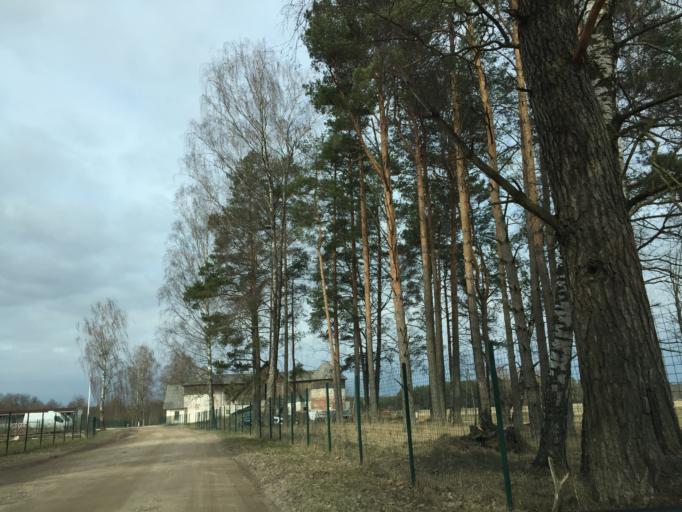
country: LV
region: Garkalne
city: Garkalne
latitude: 57.0739
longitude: 24.4457
